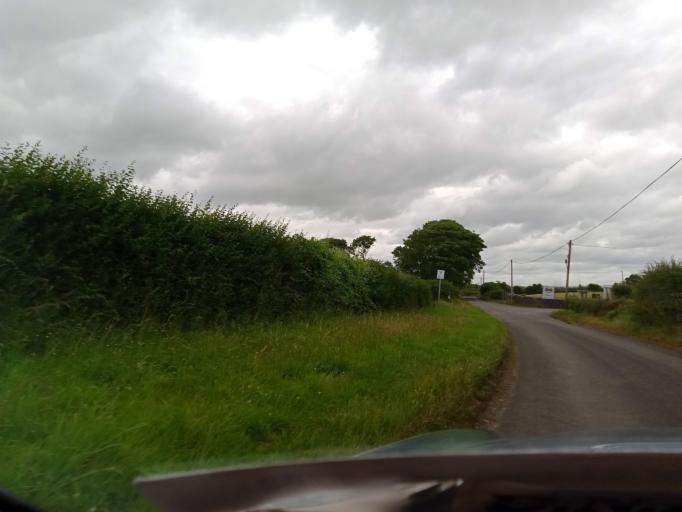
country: IE
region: Leinster
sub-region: Kilkenny
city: Thomastown
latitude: 52.5625
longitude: -7.1979
